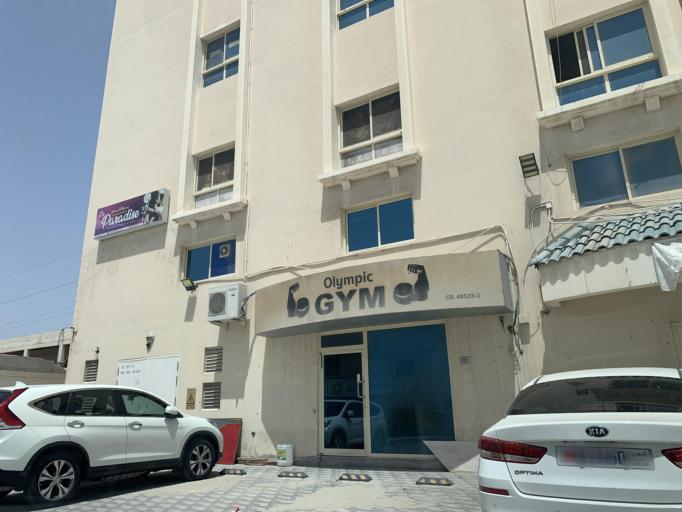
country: BH
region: Northern
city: Sitrah
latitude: 26.1743
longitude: 50.6039
